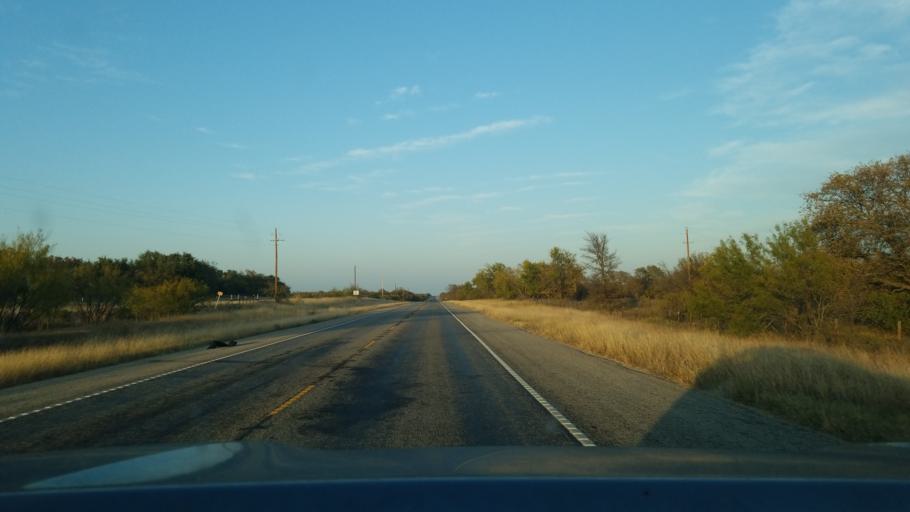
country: US
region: Texas
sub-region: Eastland County
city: Cisco
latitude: 32.4163
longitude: -98.9412
